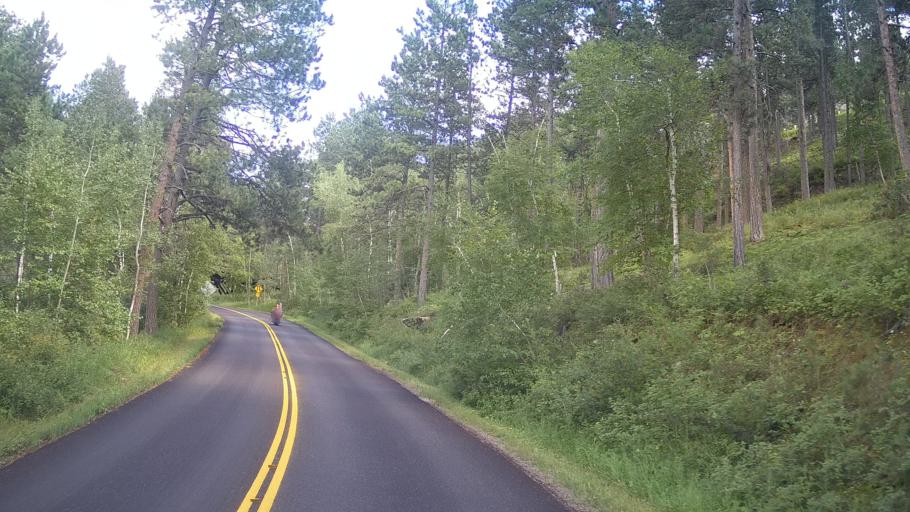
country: US
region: South Dakota
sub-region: Pennington County
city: Colonial Pine Hills
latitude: 43.8696
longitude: -103.4377
